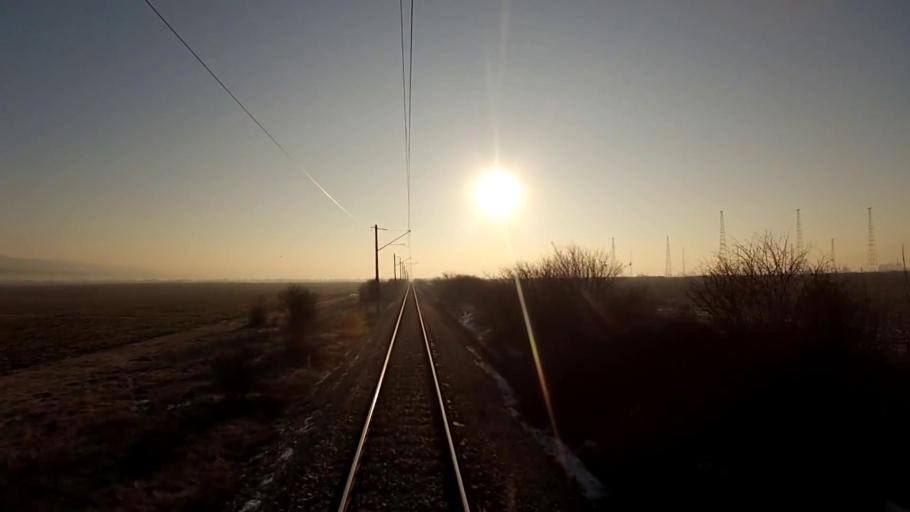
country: BG
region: Sofiya
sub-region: Obshtina Kostinbrod
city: Kostinbrod
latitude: 42.8121
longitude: 23.1912
